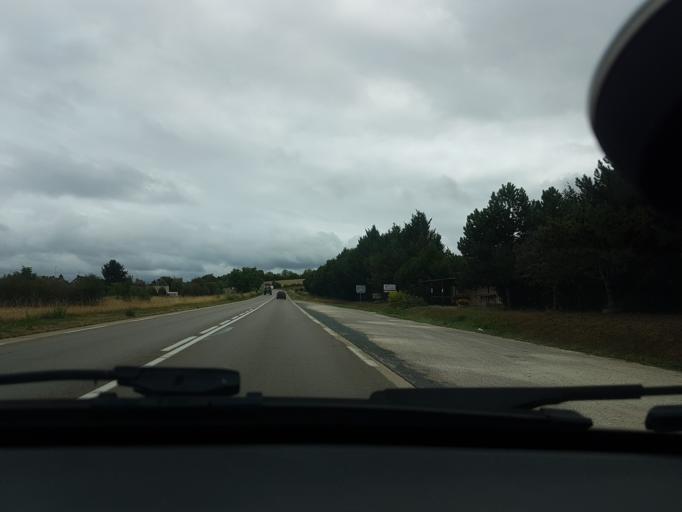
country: FR
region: Bourgogne
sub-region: Departement de l'Yonne
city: Champs-sur-Yonne
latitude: 47.7008
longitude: 3.6299
